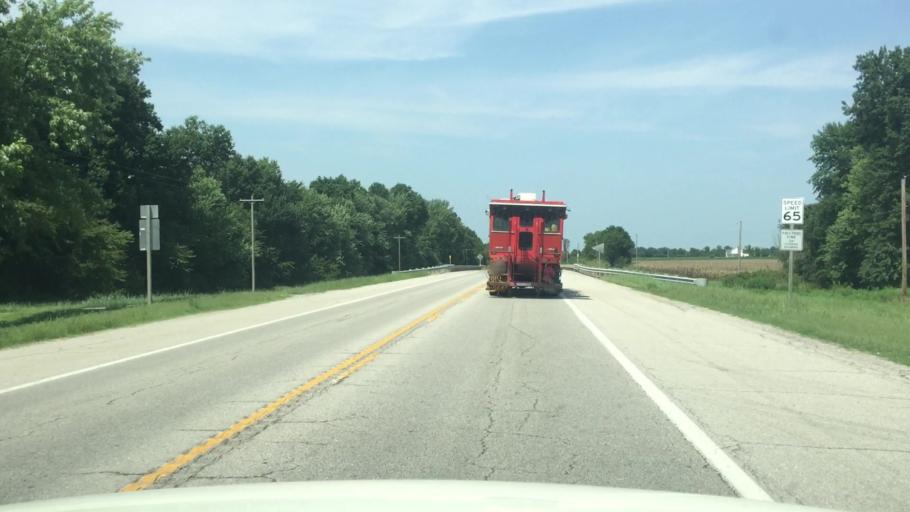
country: US
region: Kansas
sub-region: Cherokee County
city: Galena
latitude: 37.1817
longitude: -94.7045
